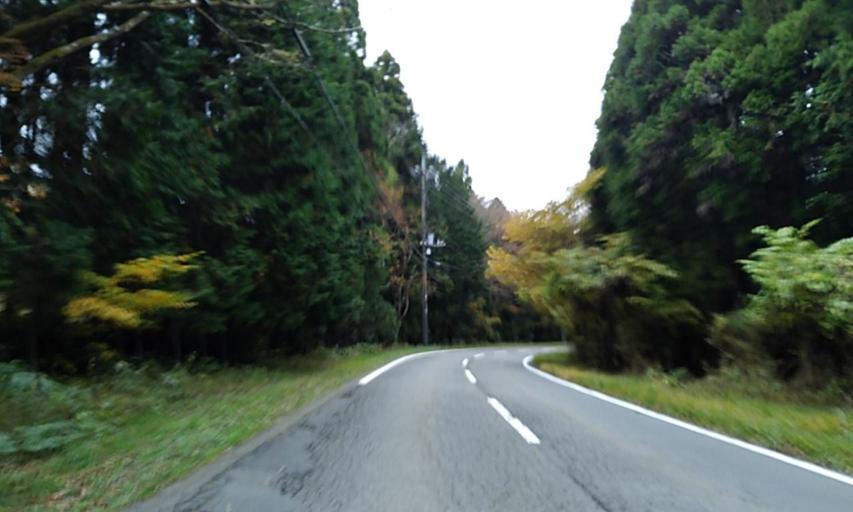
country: JP
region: Shizuoka
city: Gotemba
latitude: 35.2608
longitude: 138.8115
